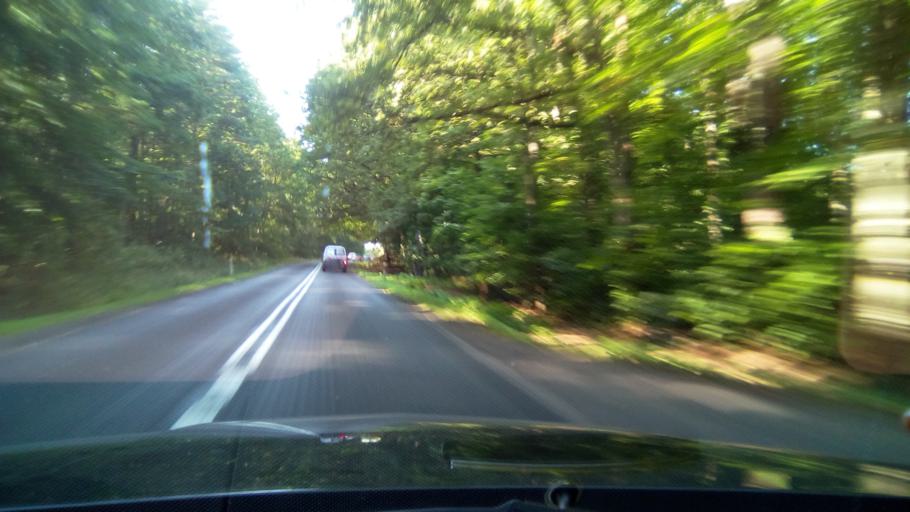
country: PL
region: West Pomeranian Voivodeship
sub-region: Powiat kamienski
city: Golczewo
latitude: 53.8086
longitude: 15.0076
